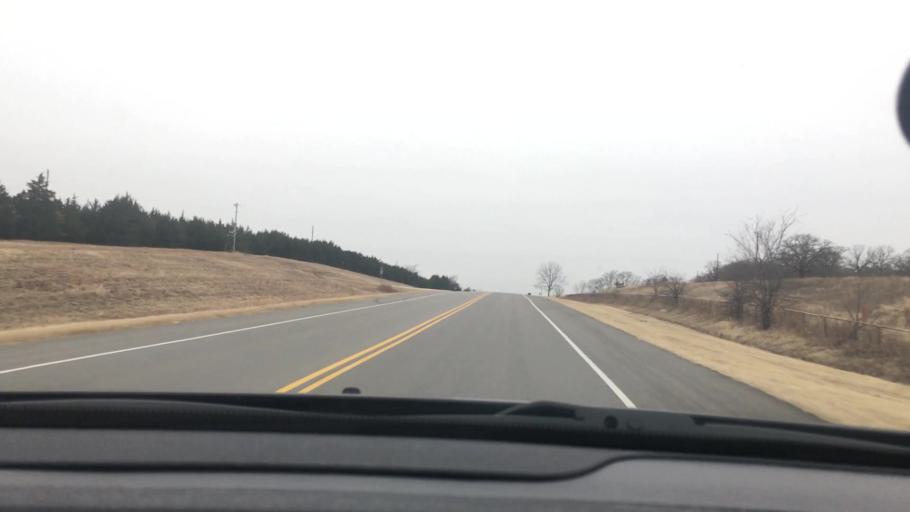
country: US
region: Oklahoma
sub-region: Garvin County
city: Wynnewood
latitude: 34.6228
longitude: -97.2068
